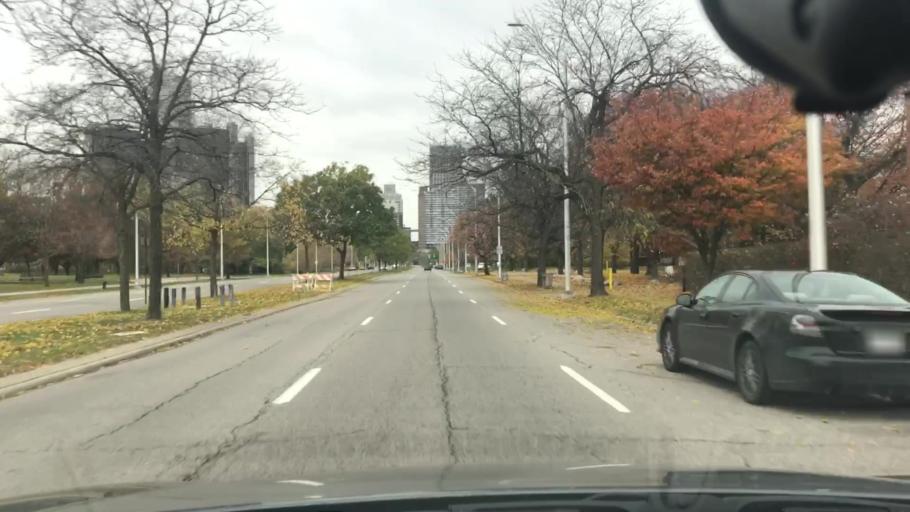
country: US
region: Michigan
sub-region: Wayne County
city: Detroit
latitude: 42.3358
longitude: -83.0308
